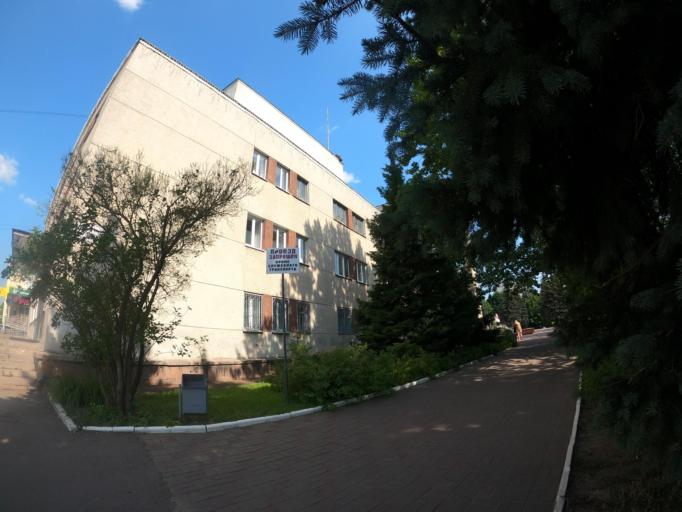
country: RU
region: Kaluga
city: Obninsk
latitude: 55.1098
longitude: 36.5901
